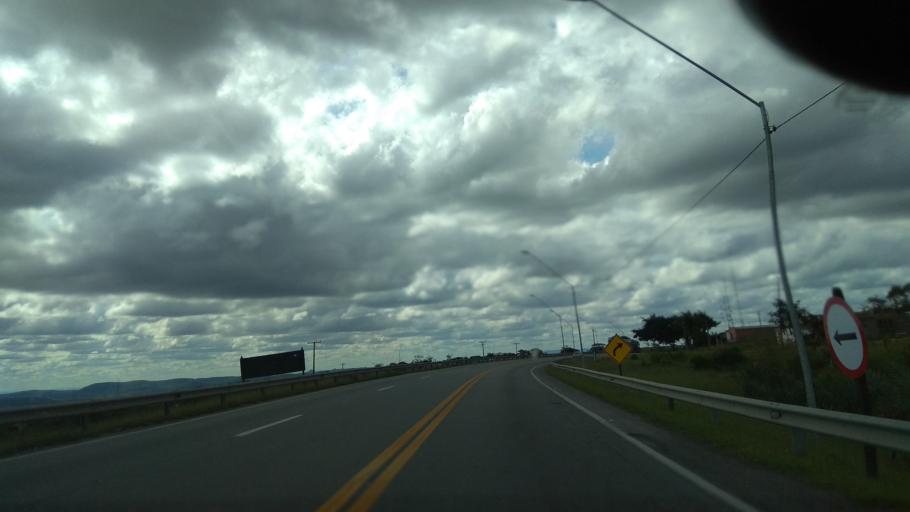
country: BR
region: Bahia
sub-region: Santa Ines
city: Santa Ines
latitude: -13.0686
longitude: -39.9609
